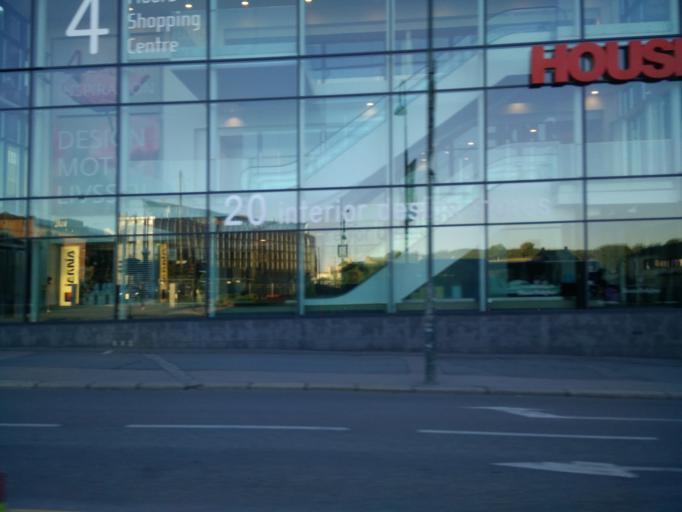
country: NO
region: Oslo
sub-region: Oslo
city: Oslo
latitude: 59.9120
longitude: 10.7266
